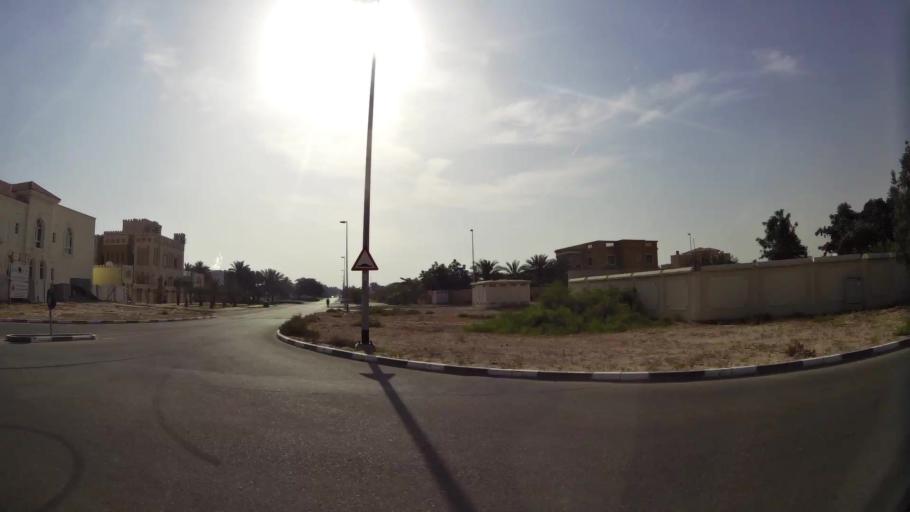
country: AE
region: Ash Shariqah
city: Sharjah
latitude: 25.2478
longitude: 55.4067
